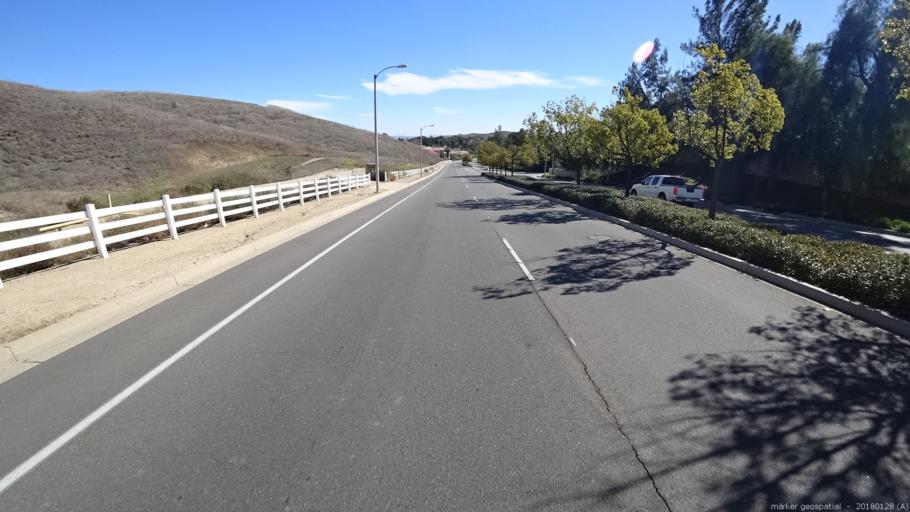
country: US
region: California
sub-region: San Bernardino County
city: Chino Hills
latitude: 33.9988
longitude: -117.7634
